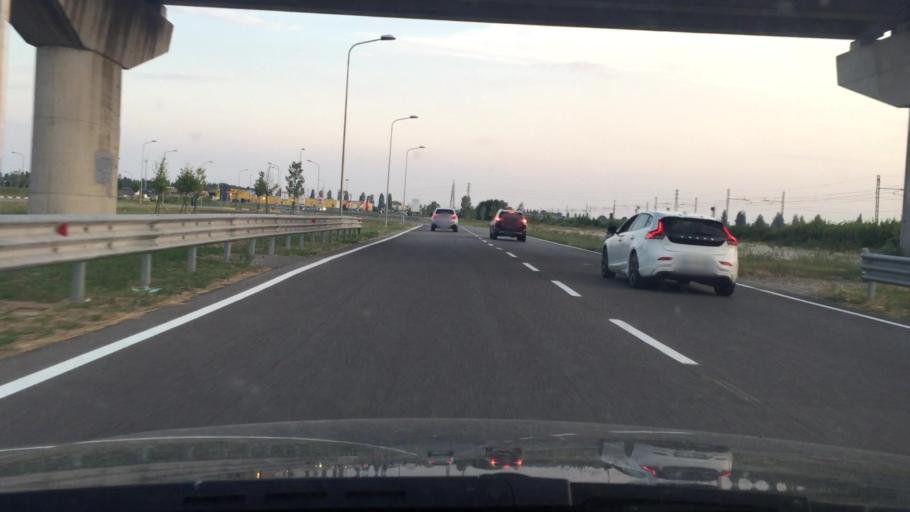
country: IT
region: Emilia-Romagna
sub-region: Provincia di Ferrara
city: Ferrara
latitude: 44.8245
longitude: 11.5895
